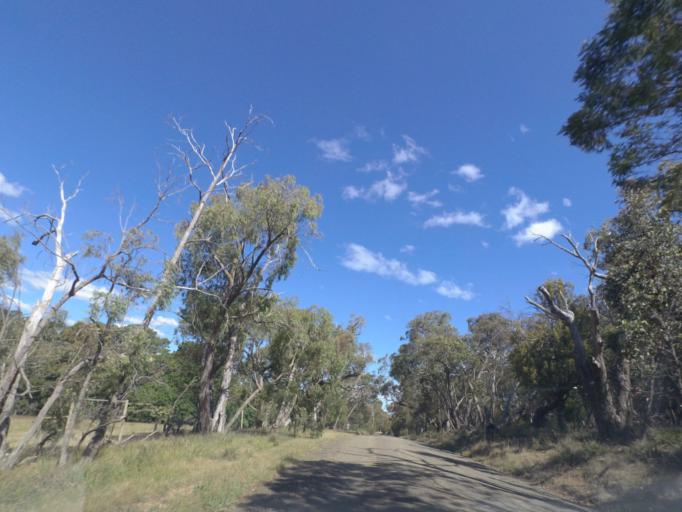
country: AU
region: Victoria
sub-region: Hume
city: Sunbury
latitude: -37.4361
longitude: 144.6627
